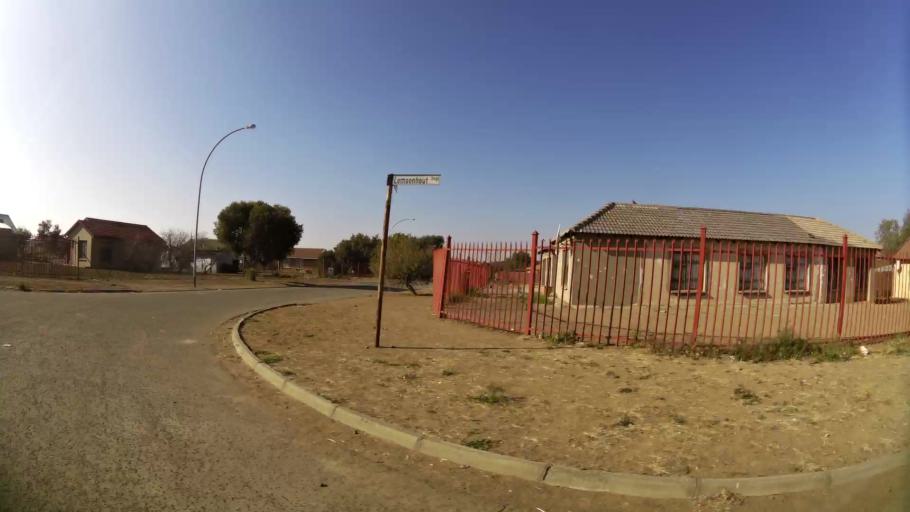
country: ZA
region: Orange Free State
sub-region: Mangaung Metropolitan Municipality
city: Bloemfontein
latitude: -29.1829
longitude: 26.1732
